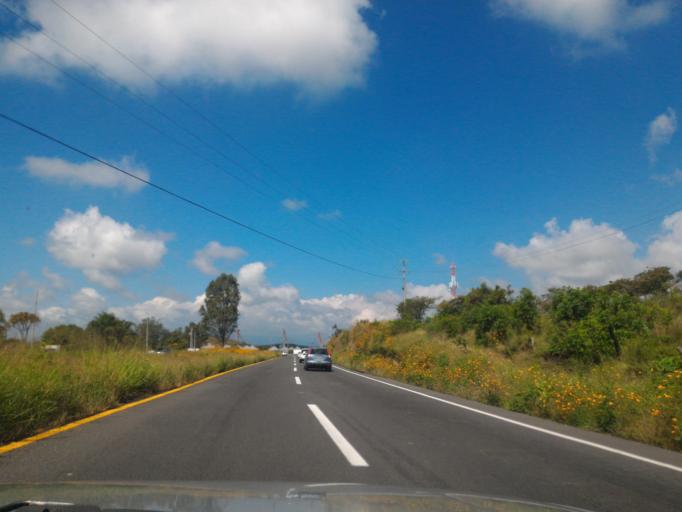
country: MX
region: Jalisco
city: La Venta del Astillero
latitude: 20.7369
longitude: -103.5862
